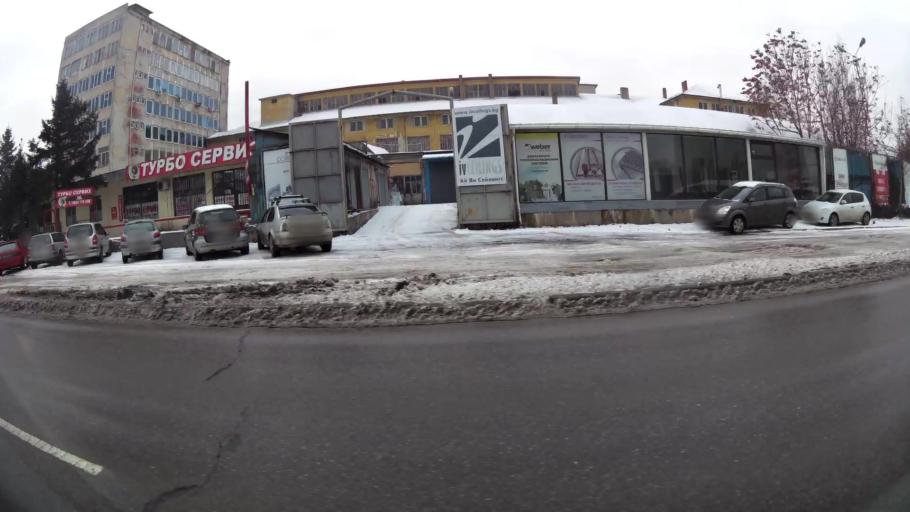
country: BG
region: Sofia-Capital
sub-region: Stolichna Obshtina
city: Sofia
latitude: 42.7166
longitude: 23.3209
